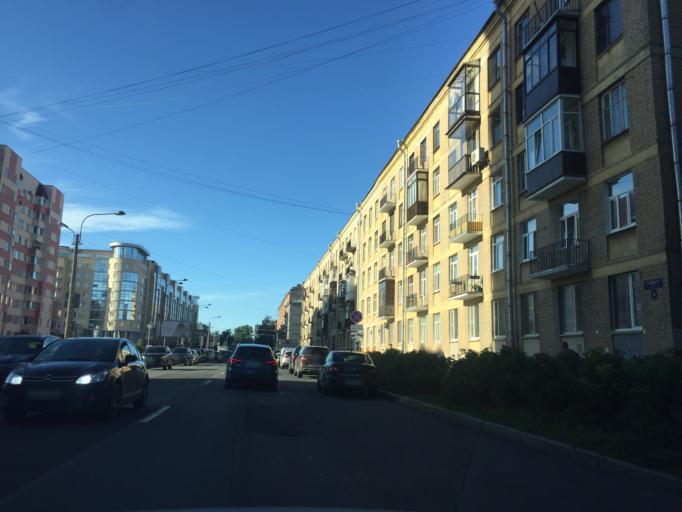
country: RU
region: St.-Petersburg
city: Admiralteisky
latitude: 59.8741
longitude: 30.3136
